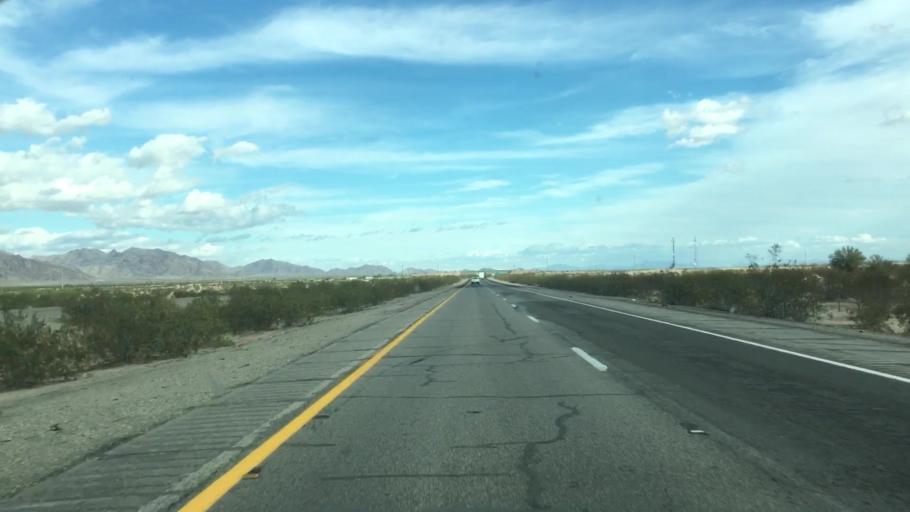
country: US
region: California
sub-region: Riverside County
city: Mesa Verde
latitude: 33.6067
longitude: -114.9158
